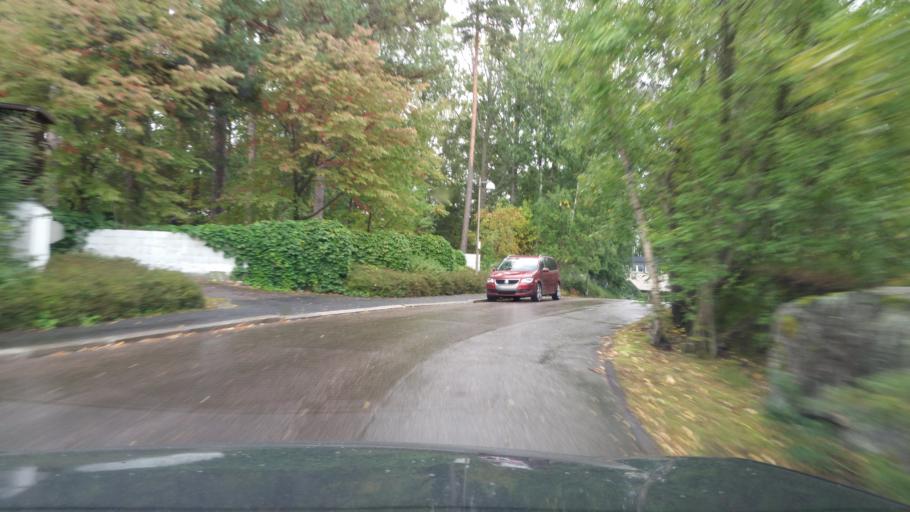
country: FI
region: Uusimaa
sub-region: Helsinki
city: Teekkarikylae
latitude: 60.1879
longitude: 24.8655
